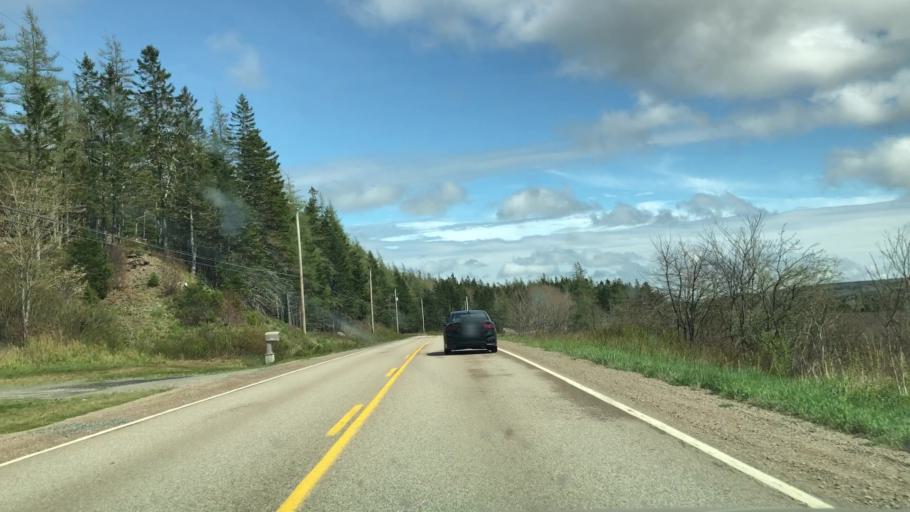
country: CA
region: Nova Scotia
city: Antigonish
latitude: 45.1919
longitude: -61.9927
